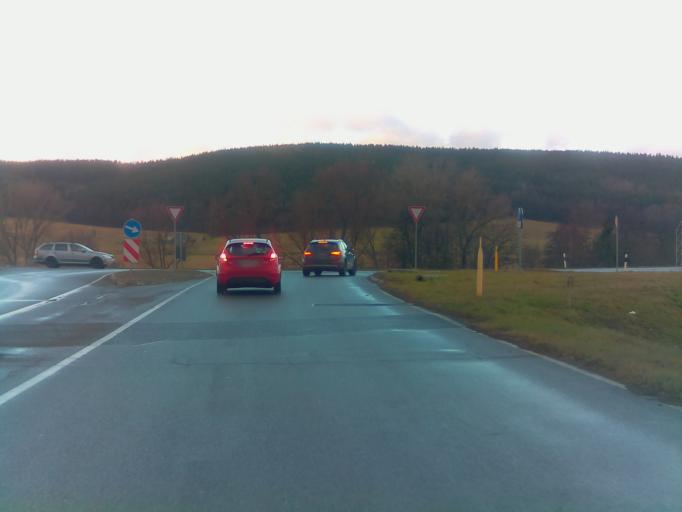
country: DE
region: Thuringia
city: Unterwellenborn
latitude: 50.6591
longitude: 11.4491
